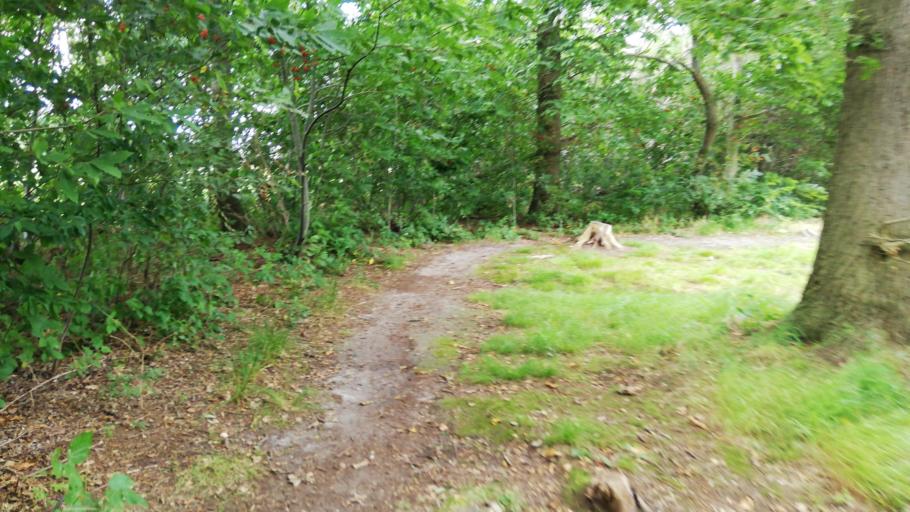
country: BE
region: Flanders
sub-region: Provincie West-Vlaanderen
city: Jabbeke
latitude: 51.1712
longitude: 3.0817
